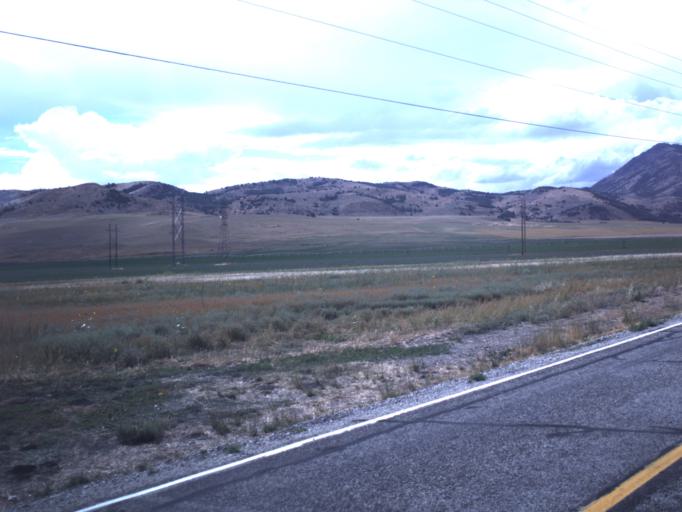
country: US
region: Utah
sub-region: Cache County
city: Benson
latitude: 41.8774
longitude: -112.0226
